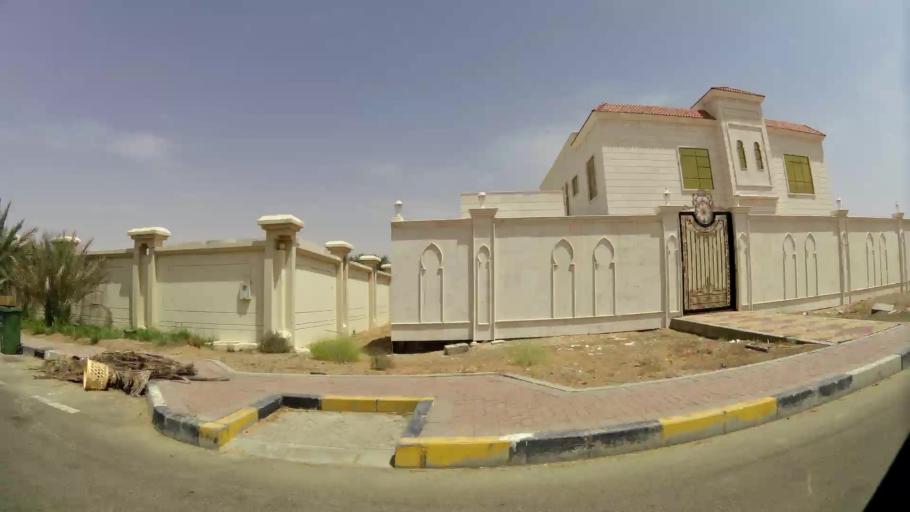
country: AE
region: Abu Dhabi
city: Al Ain
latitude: 24.1785
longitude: 55.7109
